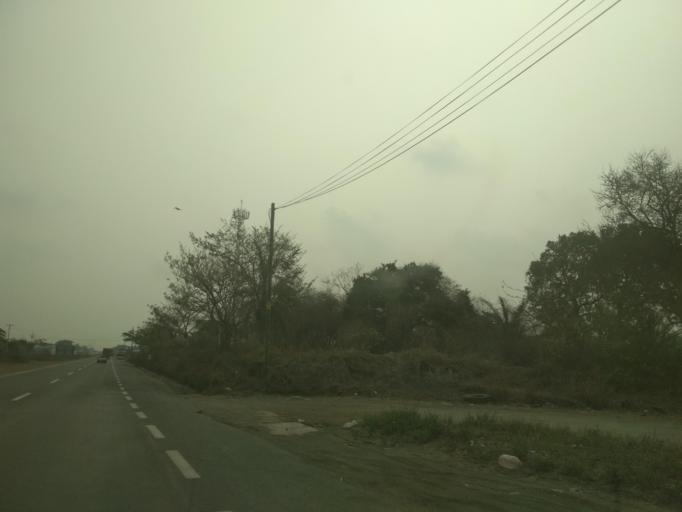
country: MX
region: Veracruz
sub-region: Veracruz
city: Delfino Victoria (Santa Fe)
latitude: 19.2041
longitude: -96.2666
